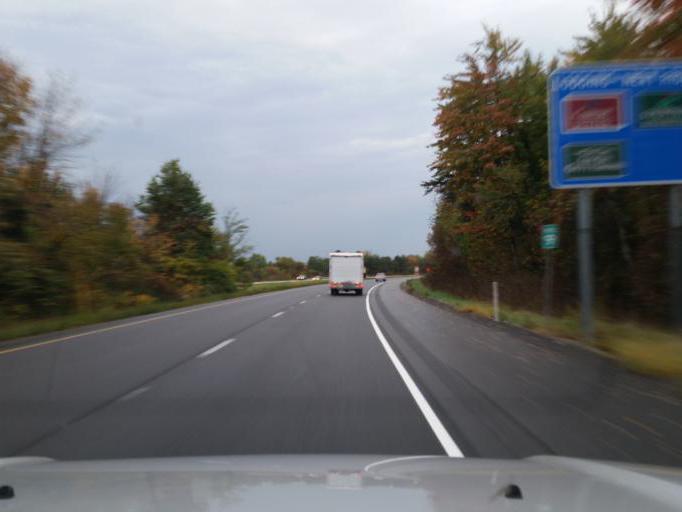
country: US
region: Pennsylvania
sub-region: Adams County
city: Lake Heritage
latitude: 39.8101
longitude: -77.1946
